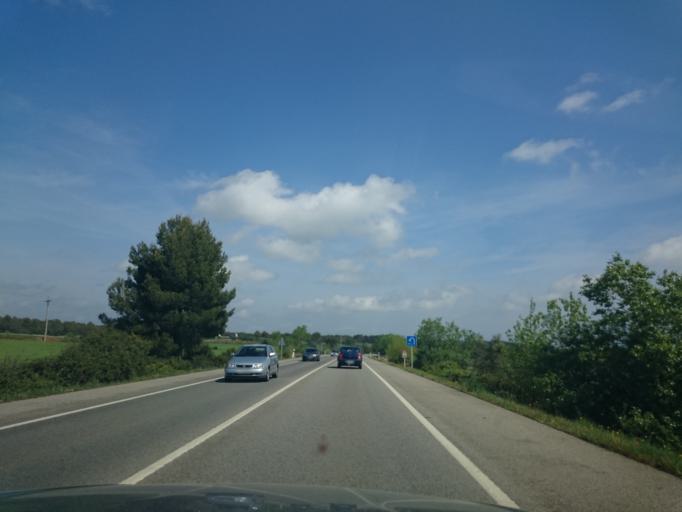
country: ES
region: Catalonia
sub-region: Provincia de Girona
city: Pontos
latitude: 42.1913
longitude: 2.9303
